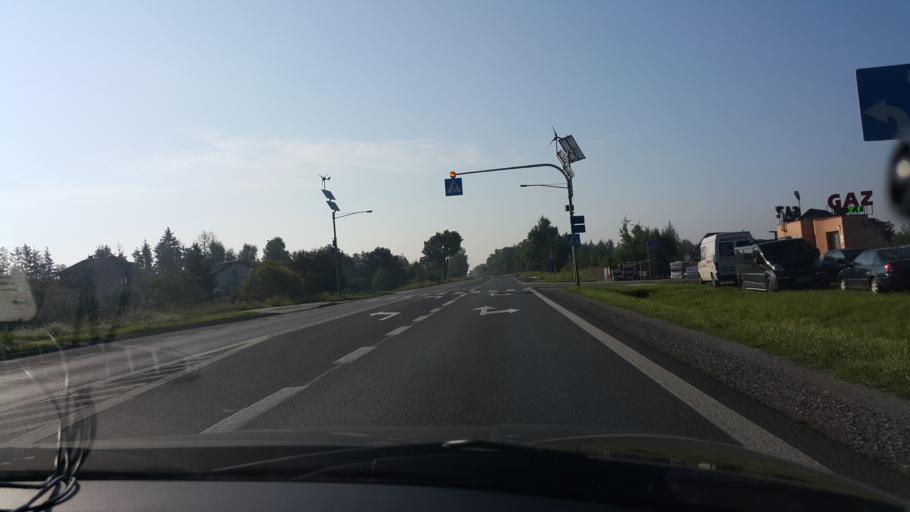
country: PL
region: Masovian Voivodeship
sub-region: Powiat radomski
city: Jedlnia-Letnisko
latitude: 51.4039
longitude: 21.2499
